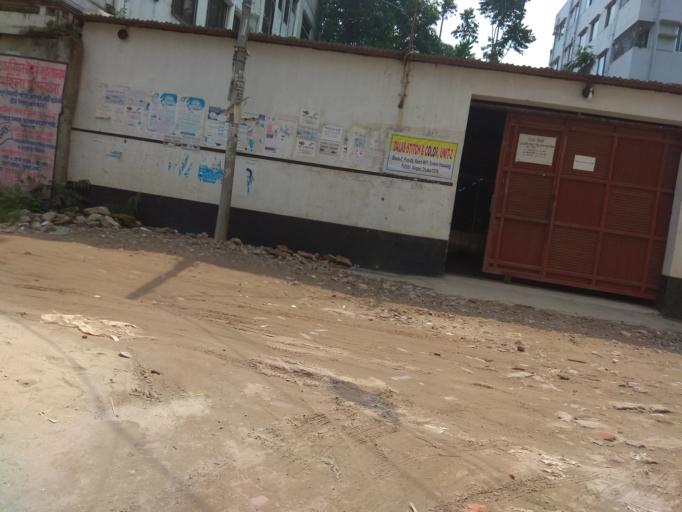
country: BD
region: Dhaka
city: Tungi
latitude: 23.8277
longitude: 90.3526
